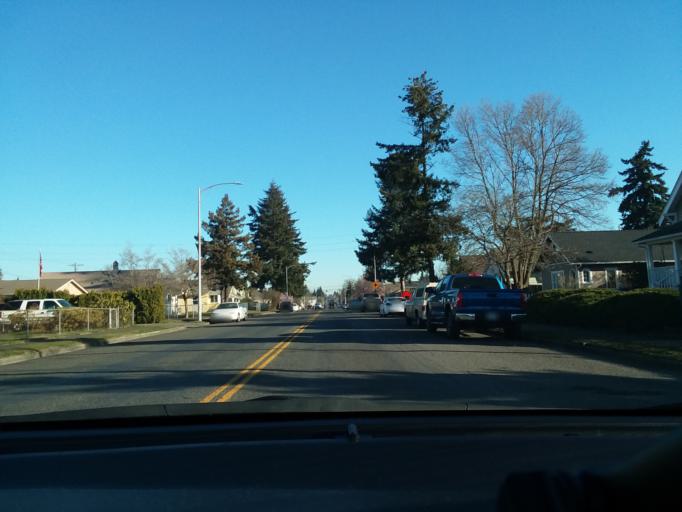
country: US
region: Washington
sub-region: Pierce County
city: Lakewood
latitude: 47.1958
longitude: -122.4723
